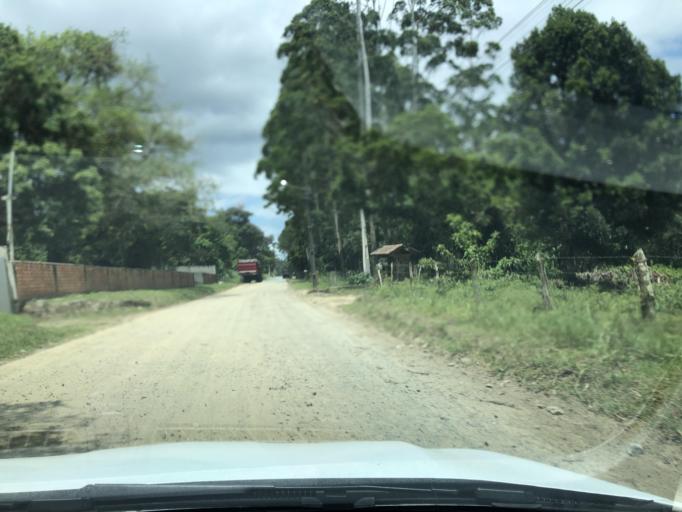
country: BR
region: Santa Catarina
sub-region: Sao Francisco Do Sul
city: Sao Francisco do Sul
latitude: -26.2260
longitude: -48.5803
